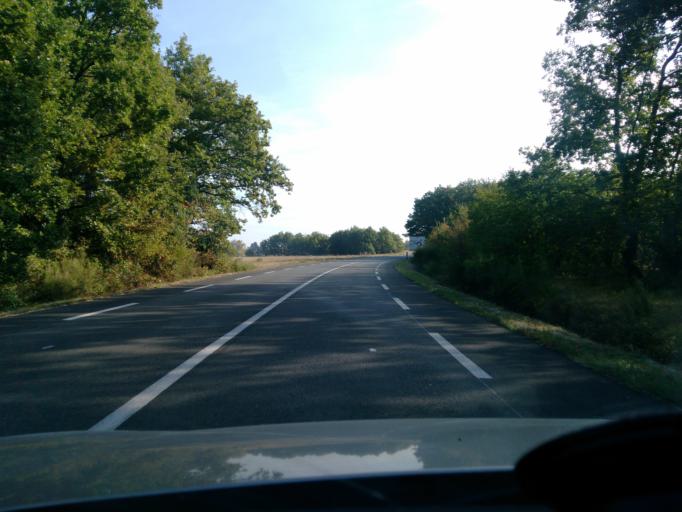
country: FR
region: Rhone-Alpes
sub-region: Departement de la Drome
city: Allan
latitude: 44.5043
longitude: 4.7865
